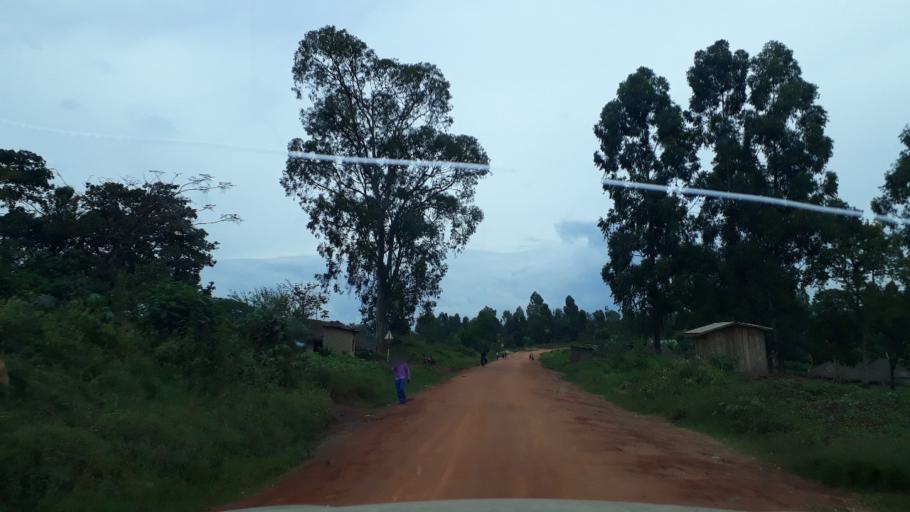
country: UG
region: Northern Region
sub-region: Zombo District
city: Paidha
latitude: 2.2208
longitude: 30.7817
